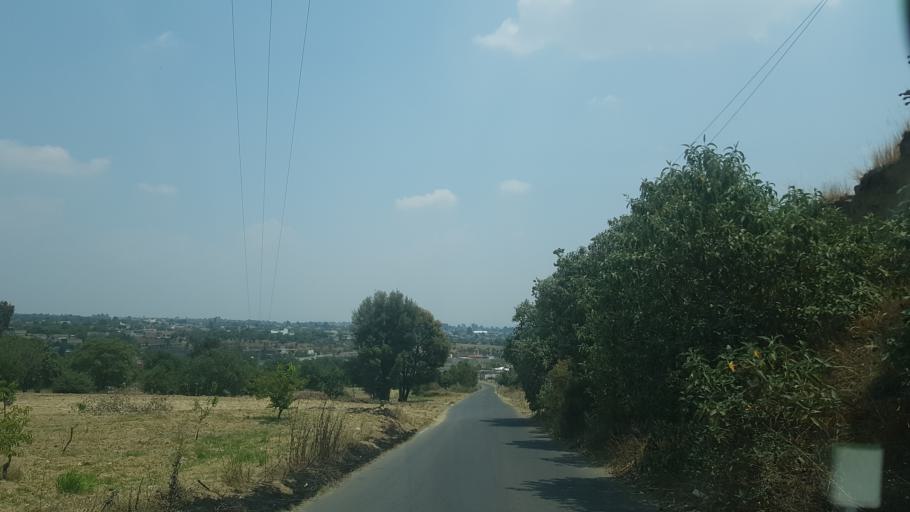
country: MX
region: Puebla
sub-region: San Nicolas de los Ranchos
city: San Pedro Yancuitlalpan
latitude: 19.0964
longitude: -98.4797
